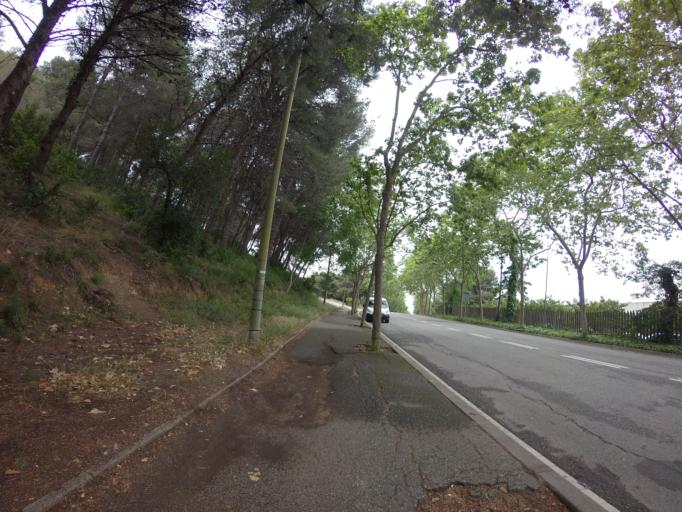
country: ES
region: Catalonia
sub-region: Provincia de Barcelona
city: Sants-Montjuic
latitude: 41.3621
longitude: 2.1614
